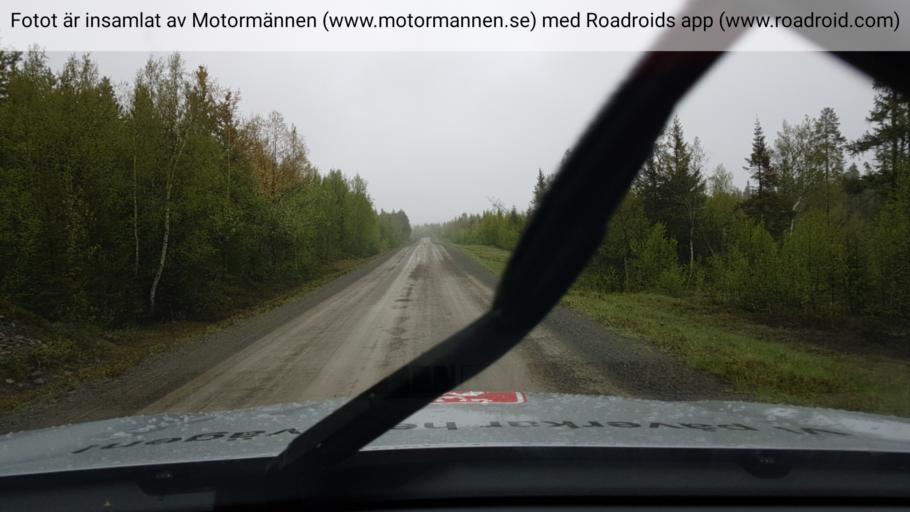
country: SE
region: Jaemtland
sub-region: Krokoms Kommun
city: Valla
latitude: 63.0529
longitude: 13.9636
